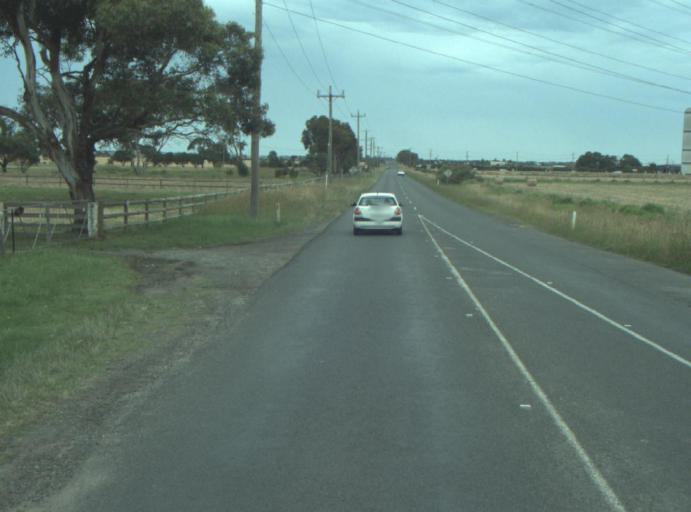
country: AU
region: Victoria
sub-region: Greater Geelong
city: Leopold
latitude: -38.1791
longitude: 144.4202
